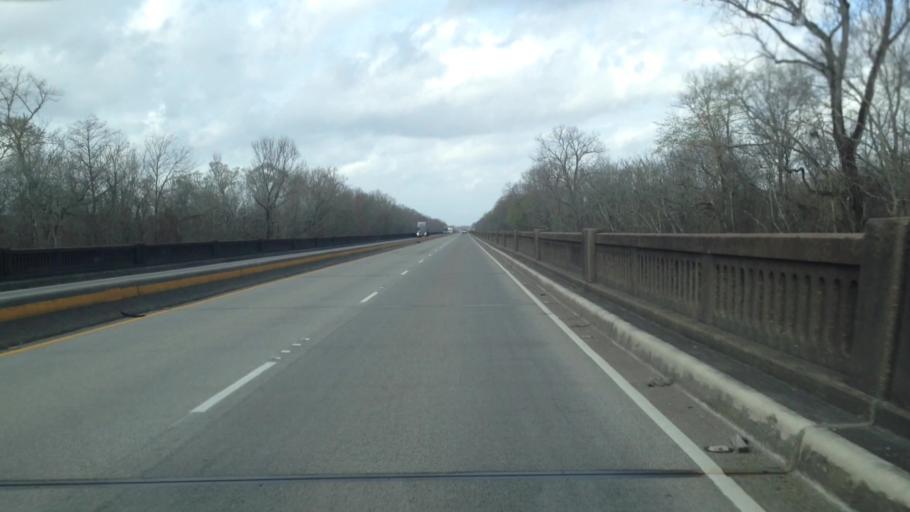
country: US
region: Louisiana
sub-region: Saint Landry Parish
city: Krotz Springs
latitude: 30.5539
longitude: -91.6997
